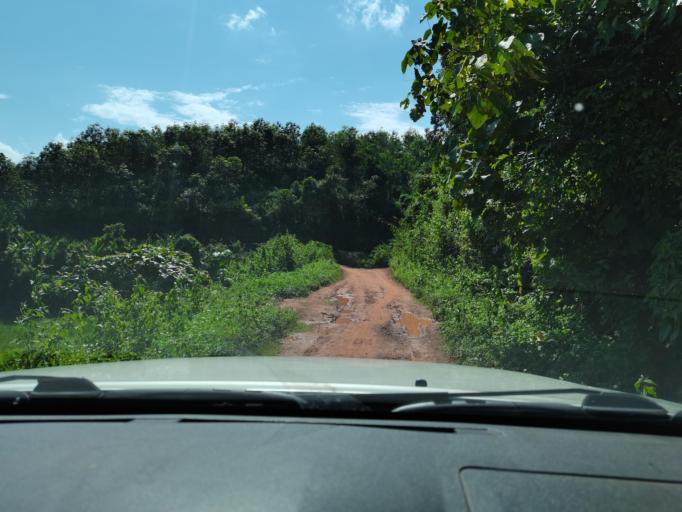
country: LA
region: Loungnamtha
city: Muang Nale
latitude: 20.5568
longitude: 101.0623
